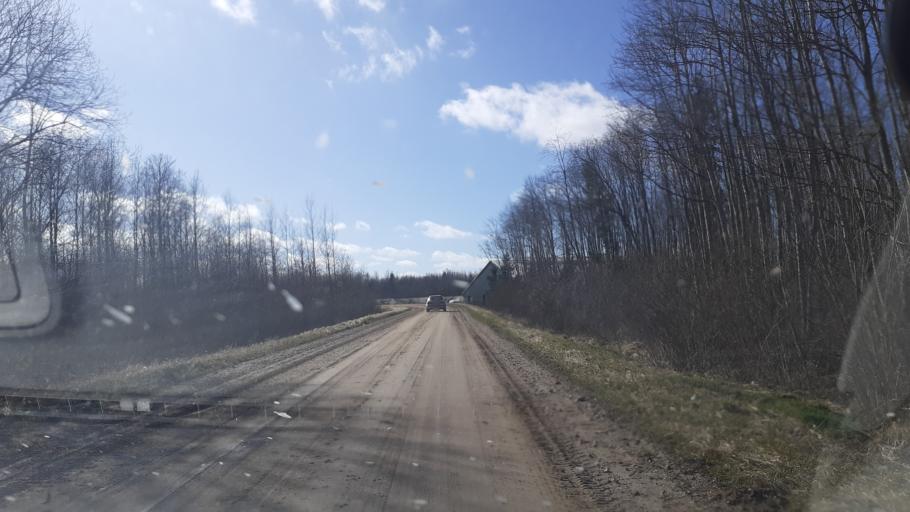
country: LV
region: Kuldigas Rajons
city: Kuldiga
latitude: 56.9231
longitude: 22.1356
